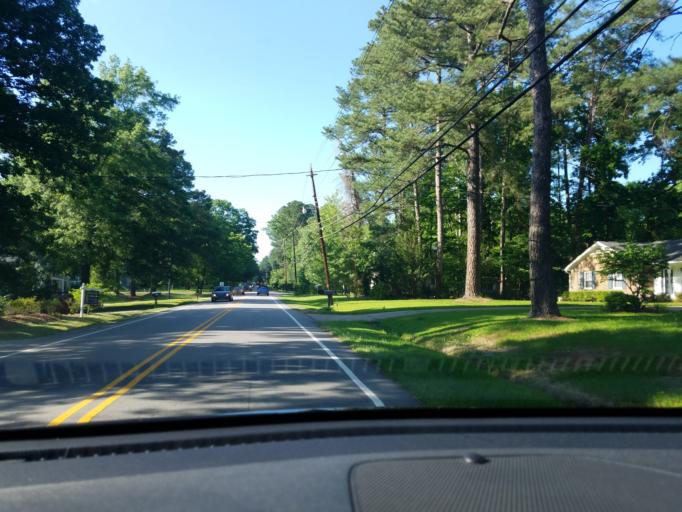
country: US
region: North Carolina
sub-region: Durham County
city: Durham
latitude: 35.9659
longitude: -78.9326
